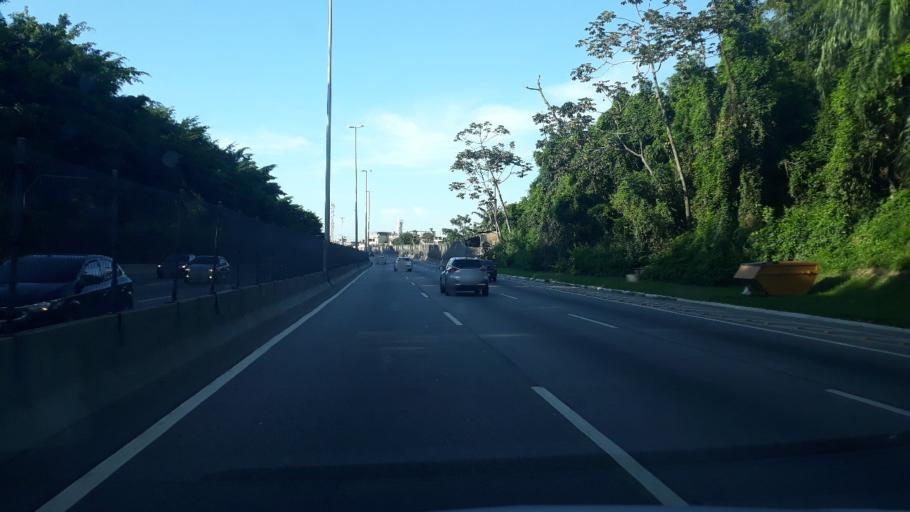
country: BR
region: Rio de Janeiro
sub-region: Sao Joao De Meriti
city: Sao Joao de Meriti
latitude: -22.9476
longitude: -43.3553
